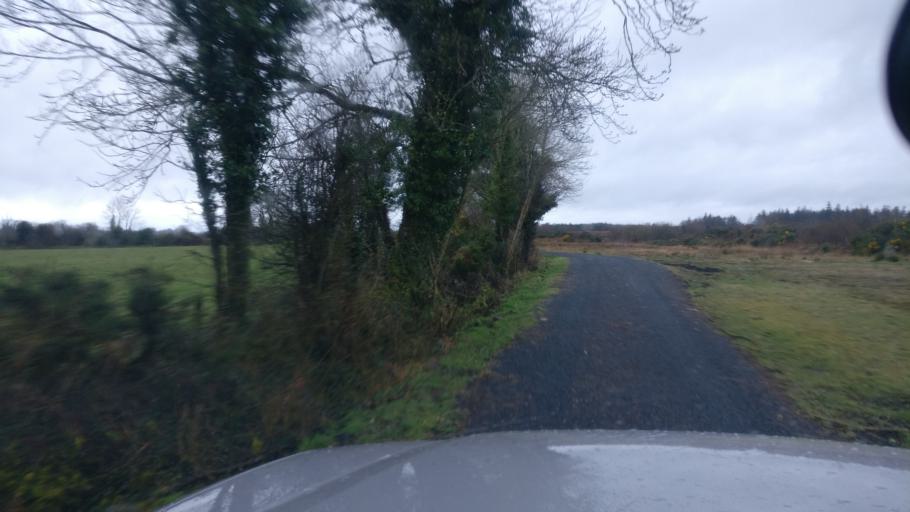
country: IE
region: Connaught
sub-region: County Galway
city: Ballinasloe
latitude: 53.2467
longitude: -8.3308
